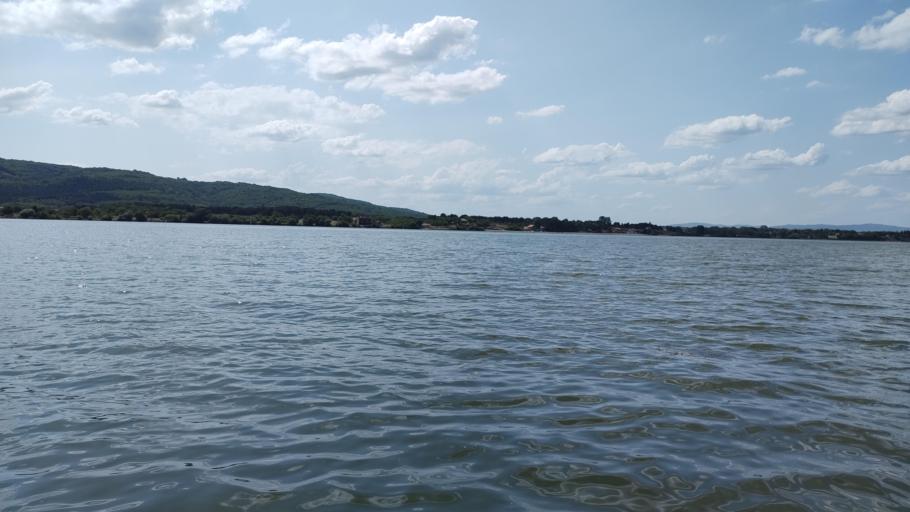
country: RS
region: Central Serbia
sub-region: Branicevski Okrug
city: Golubac
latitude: 44.6732
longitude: 21.6183
